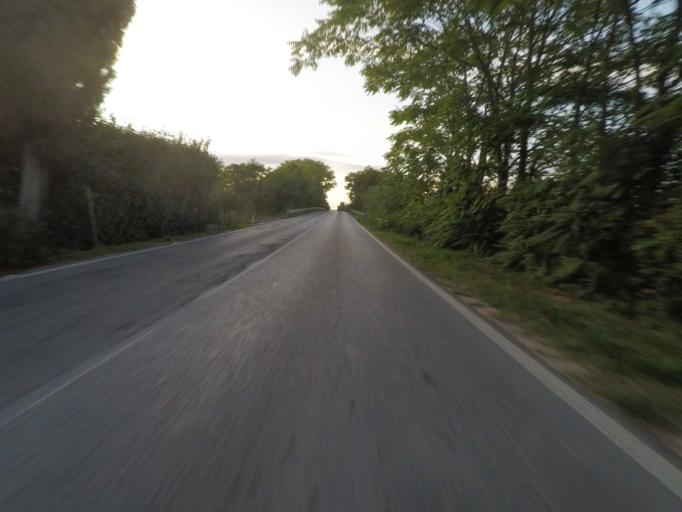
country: IT
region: Tuscany
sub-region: Provincia di Siena
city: Torrita di Siena
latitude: 43.1858
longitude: 11.7650
